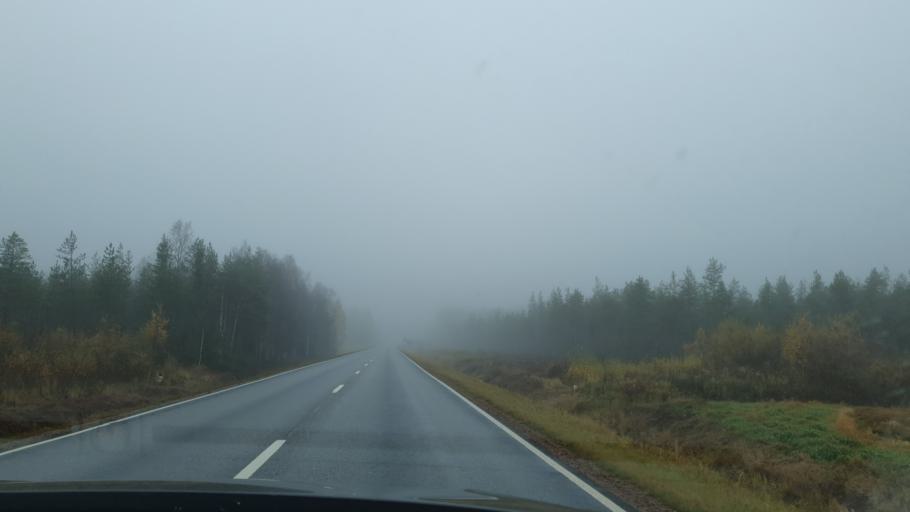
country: FI
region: Lapland
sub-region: Rovaniemi
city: Rovaniemi
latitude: 66.7975
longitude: 25.4147
